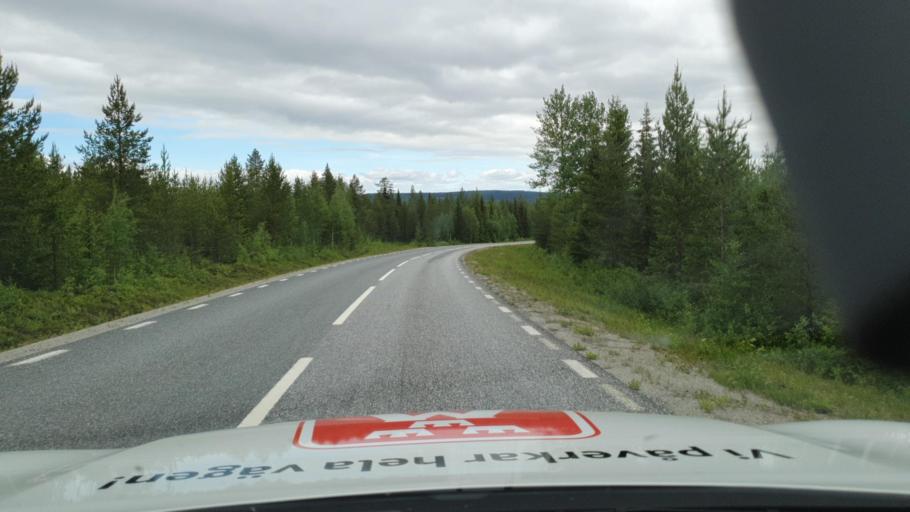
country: SE
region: Vaesterbotten
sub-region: Asele Kommun
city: Asele
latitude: 64.2054
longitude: 17.5111
